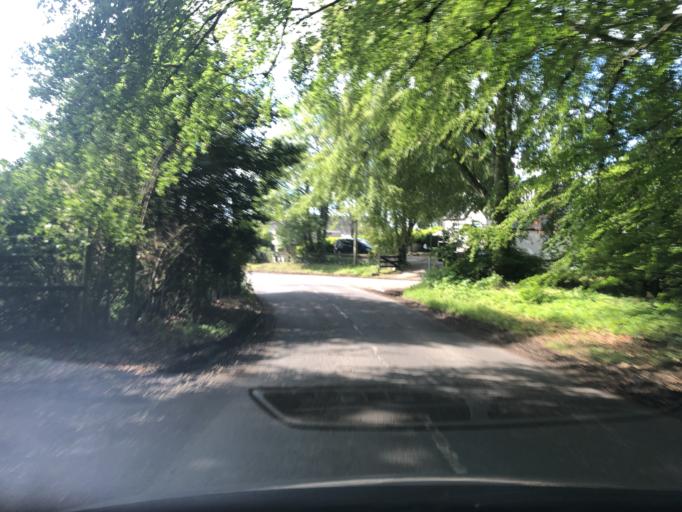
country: GB
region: Scotland
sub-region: Angus
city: Kirriemuir
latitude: 56.7303
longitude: -3.0046
